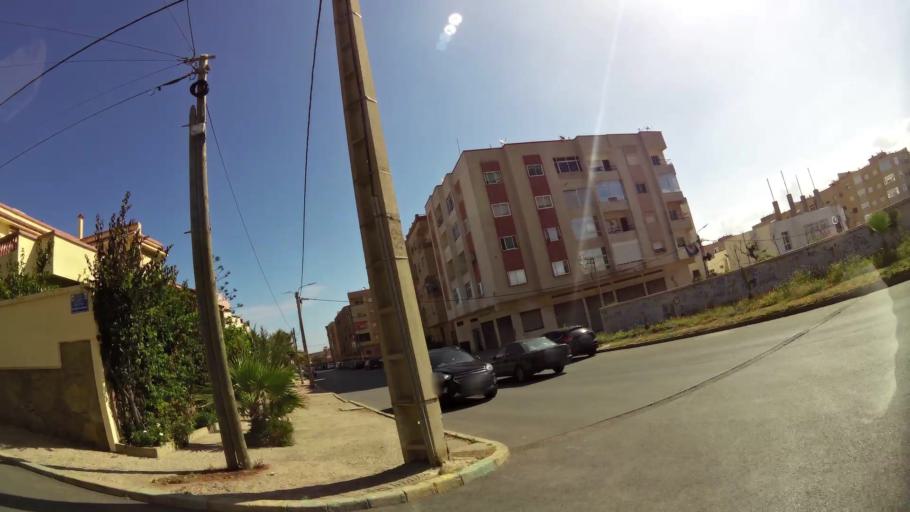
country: MA
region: Rabat-Sale-Zemmour-Zaer
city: Sale
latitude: 34.0679
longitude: -6.8034
